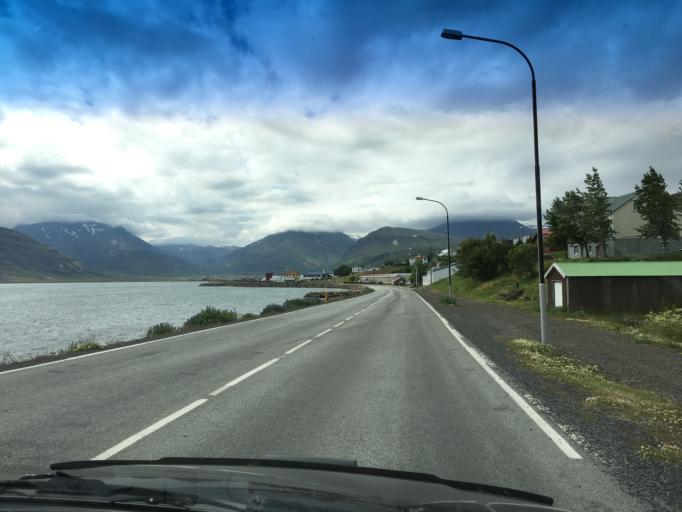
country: IS
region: East
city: Reydarfjoerdur
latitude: 65.0316
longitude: -14.1964
